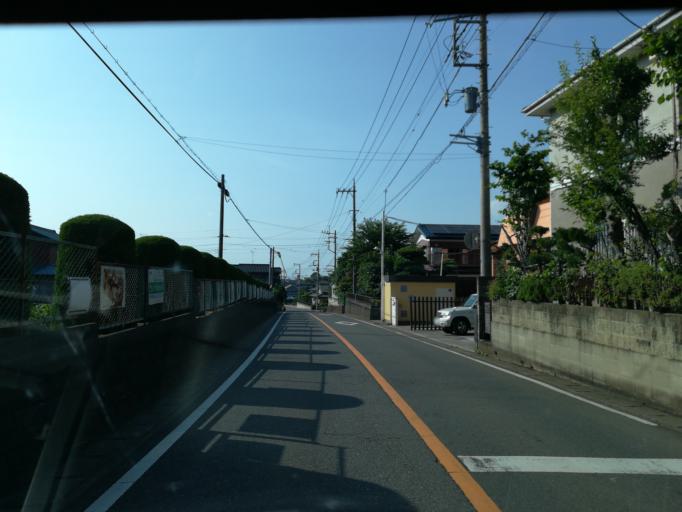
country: JP
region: Saitama
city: Tokorozawa
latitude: 35.7908
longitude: 139.4091
